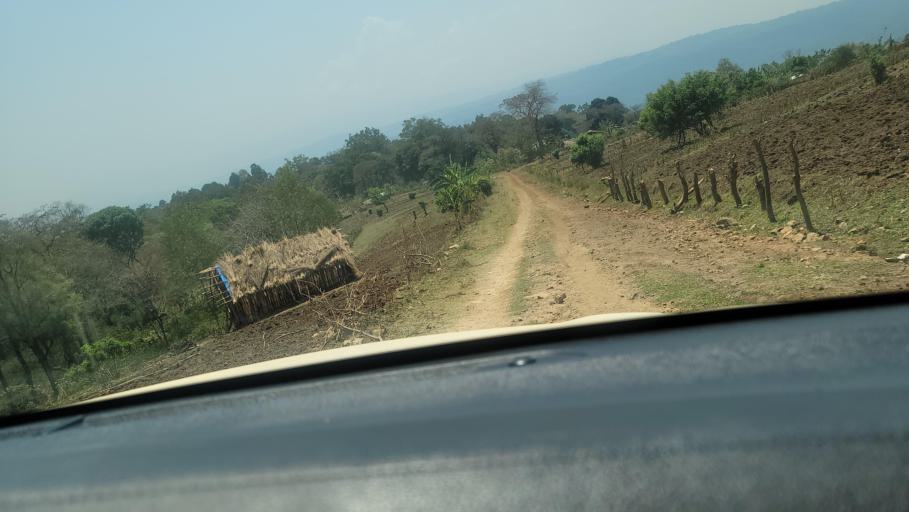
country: ET
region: Southern Nations, Nationalities, and People's Region
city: Bonga
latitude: 7.5363
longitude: 36.1844
